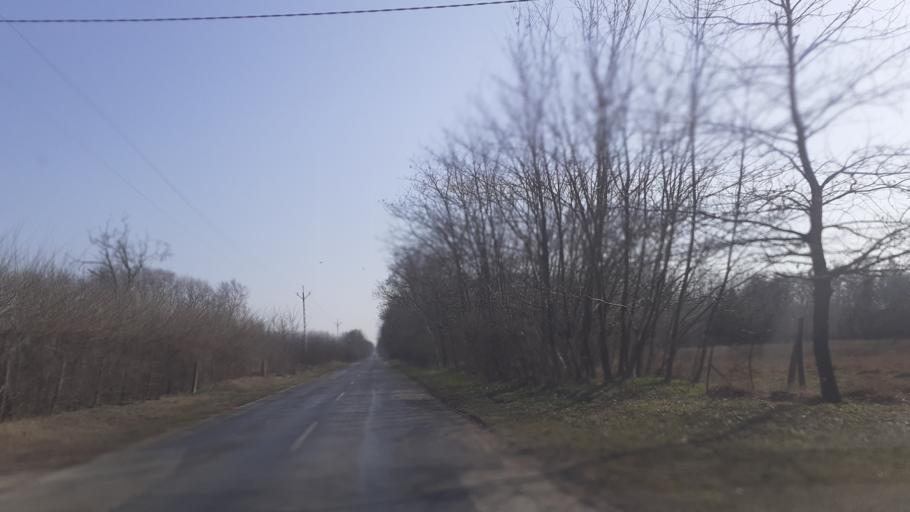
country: HU
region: Bacs-Kiskun
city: Lajosmizse
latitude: 47.0172
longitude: 19.4861
